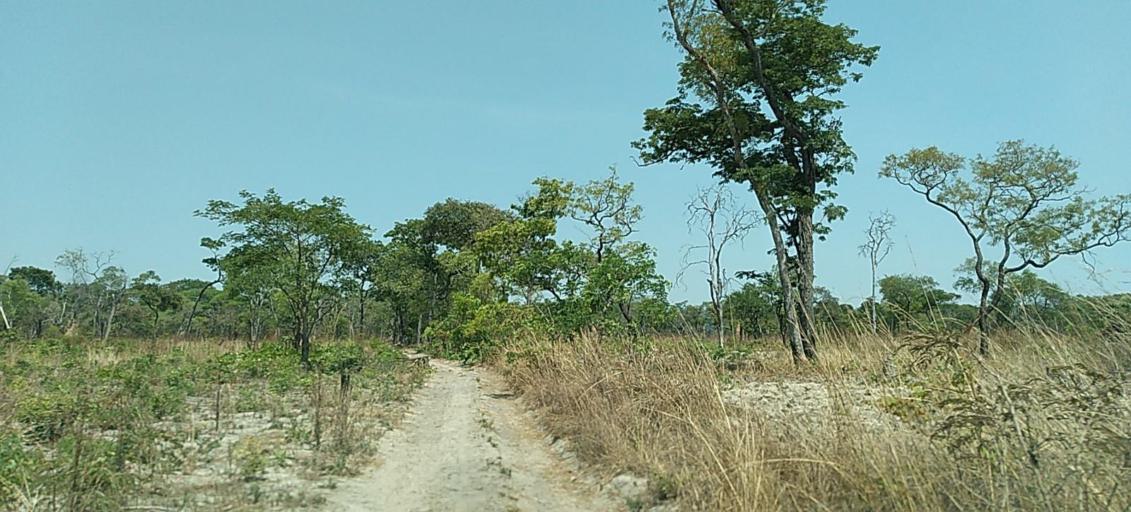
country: ZM
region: Copperbelt
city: Mpongwe
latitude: -13.7854
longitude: 28.1011
